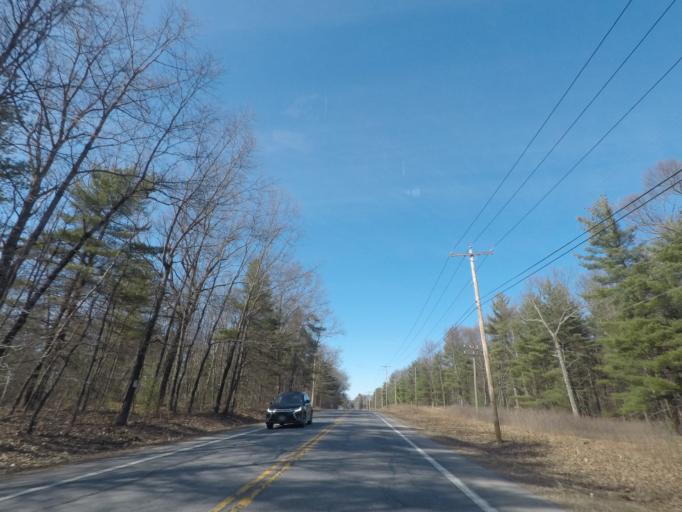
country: US
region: New York
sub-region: Saratoga County
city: Milton
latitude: 43.0553
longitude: -73.8505
